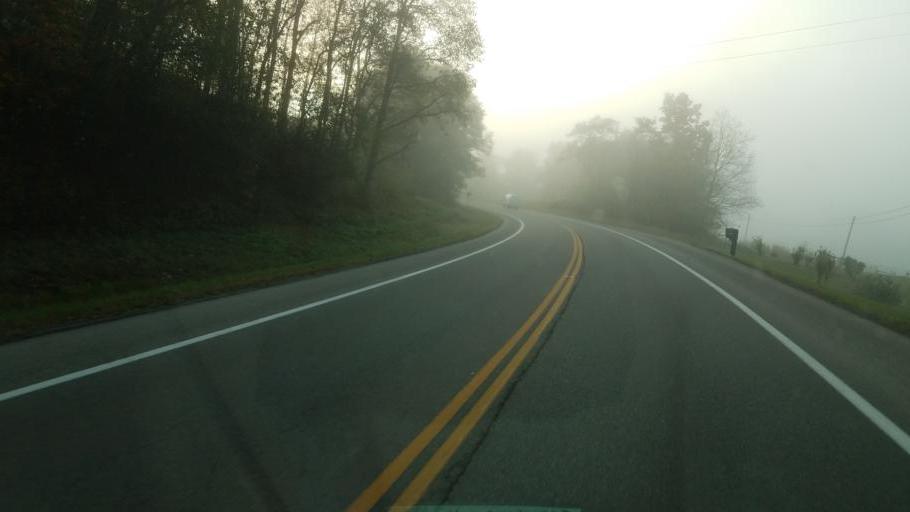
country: US
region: Ohio
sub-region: Tuscarawas County
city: Sugarcreek
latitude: 40.5170
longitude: -81.7089
